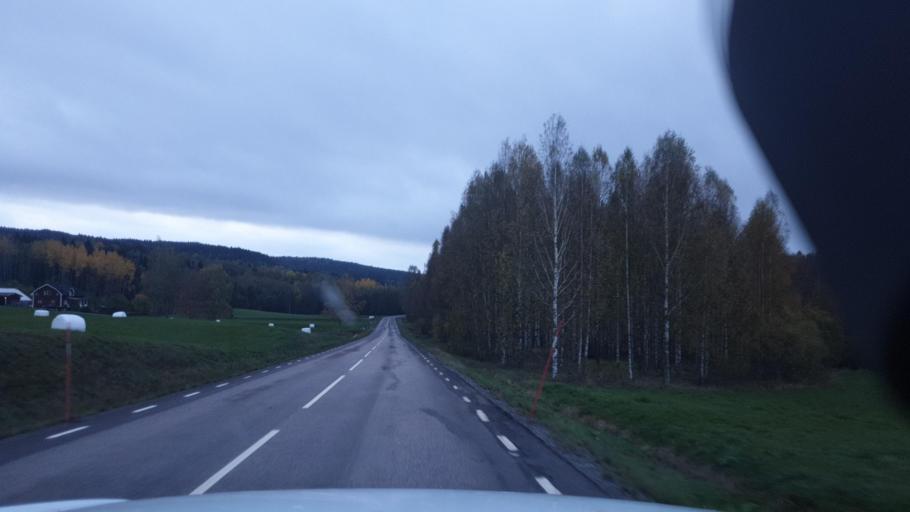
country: SE
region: Vaermland
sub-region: Arvika Kommun
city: Arvika
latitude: 59.7521
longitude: 12.6343
